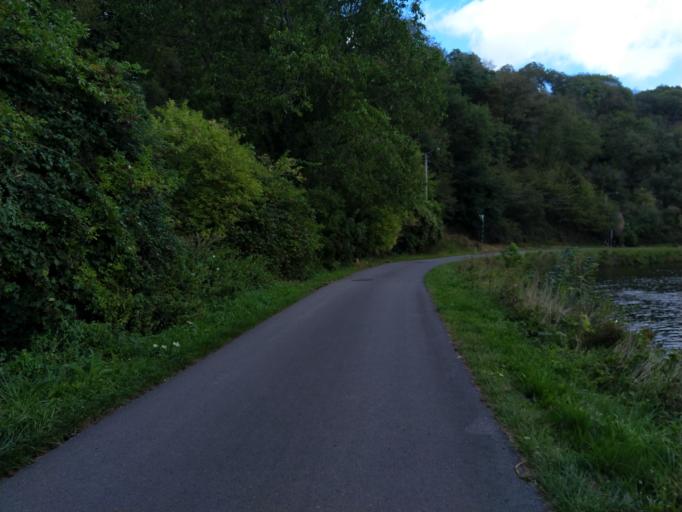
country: BE
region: Wallonia
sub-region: Province du Hainaut
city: Lobbes
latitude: 50.3477
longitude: 4.2743
